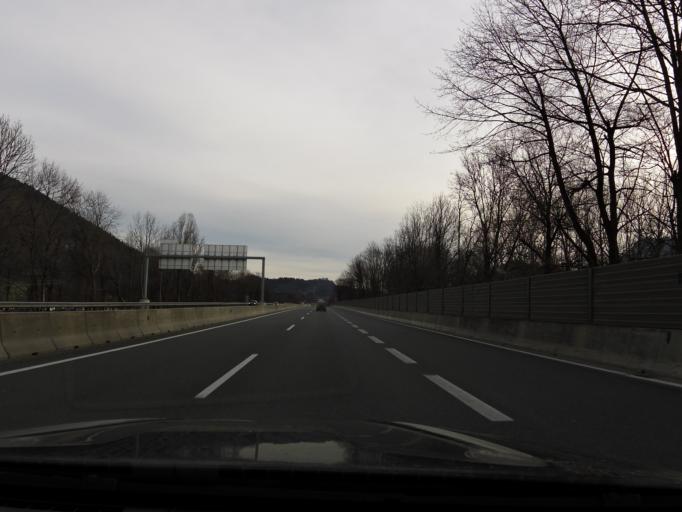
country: AT
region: Tyrol
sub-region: Politischer Bezirk Kufstein
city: Kufstein
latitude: 47.5723
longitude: 12.1443
